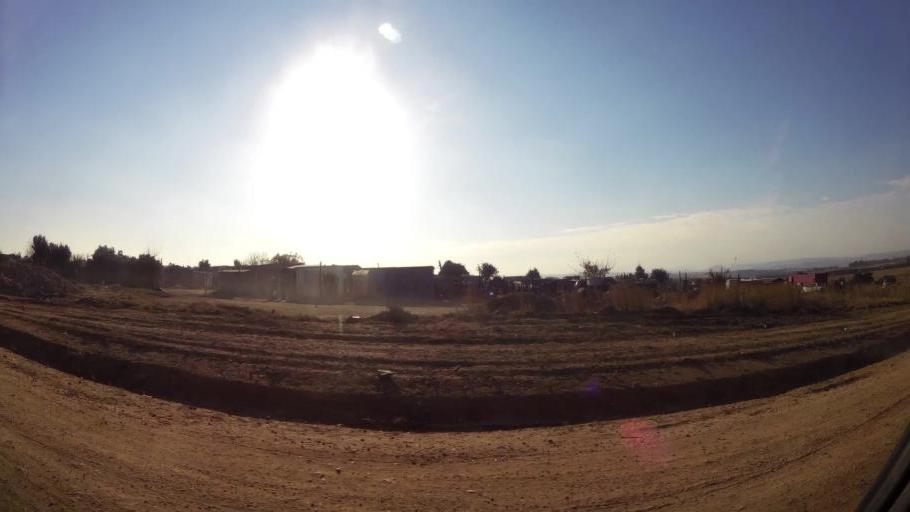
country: ZA
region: Gauteng
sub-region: City of Johannesburg Metropolitan Municipality
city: Diepsloot
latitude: -25.9893
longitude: 27.9342
